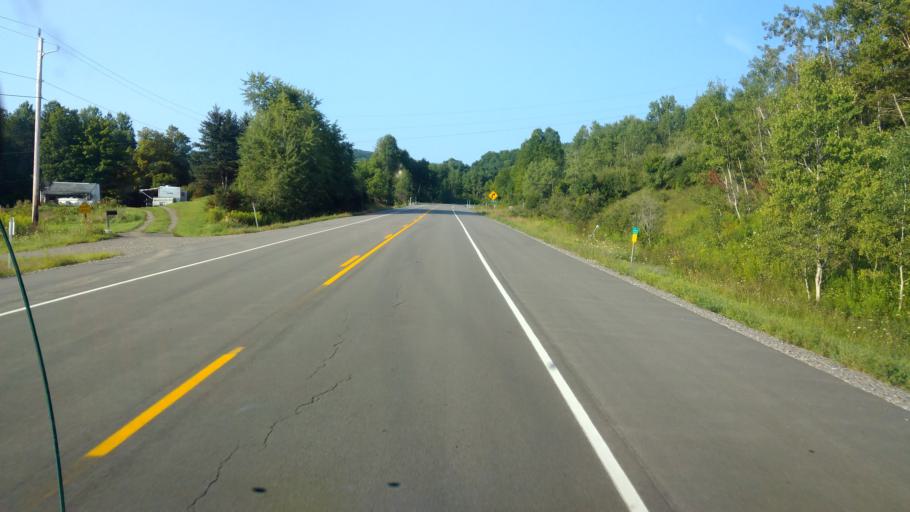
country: US
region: New York
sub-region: Steuben County
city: Canisteo
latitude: 42.1407
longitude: -77.6490
